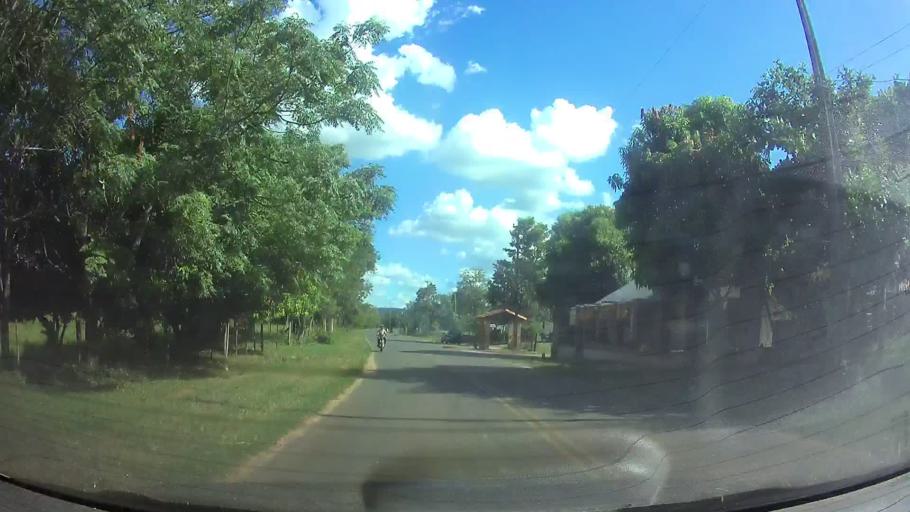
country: PY
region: Paraguari
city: Sapucai
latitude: -25.6715
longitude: -56.8620
